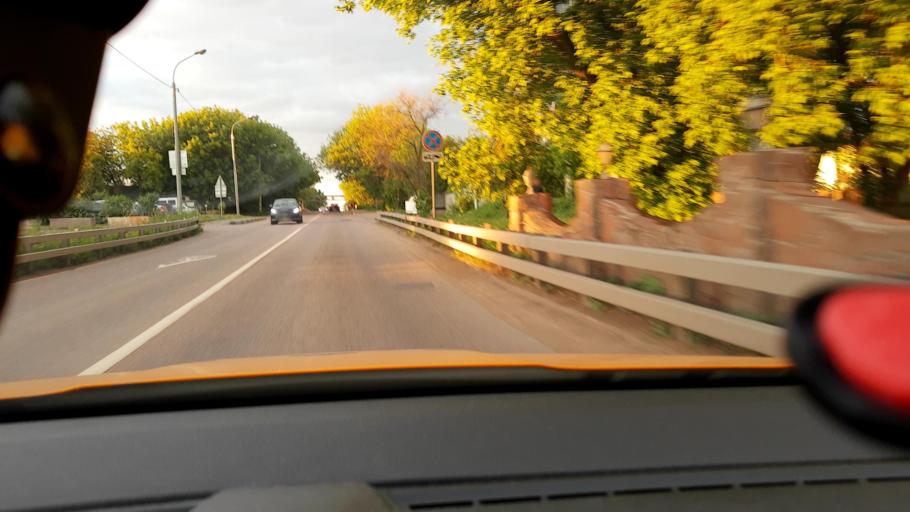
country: RU
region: Moscow
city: Khimki
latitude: 55.9035
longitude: 37.4257
